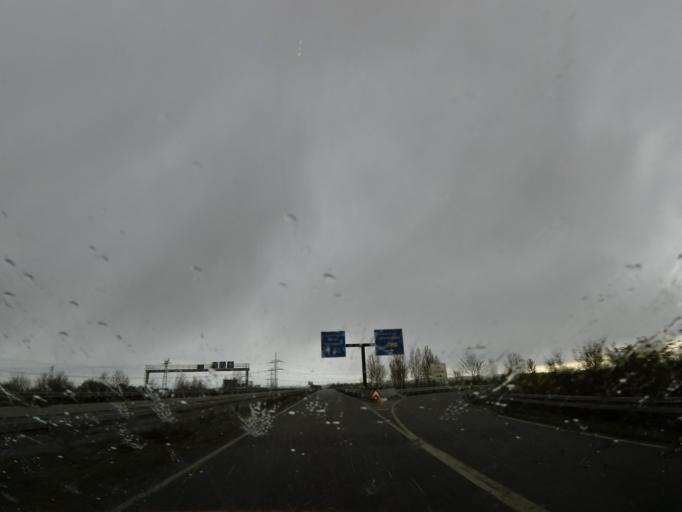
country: DE
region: Saxony-Anhalt
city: Diesdorf
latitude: 52.0721
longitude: 11.5551
